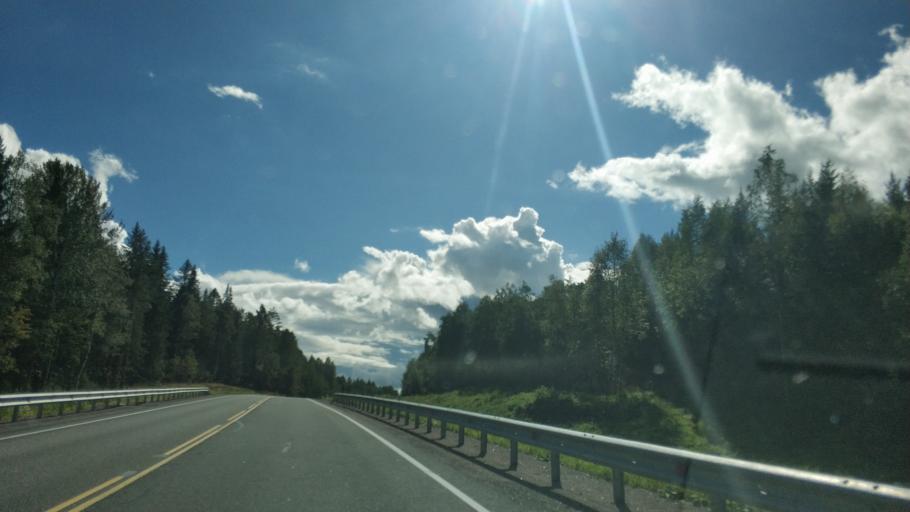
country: RU
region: Republic of Karelia
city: Khelyulya
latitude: 61.8522
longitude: 30.6504
